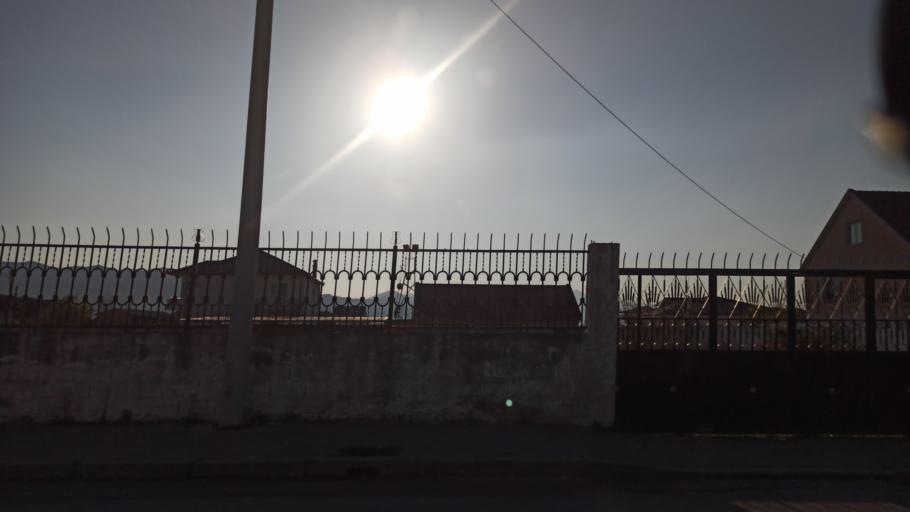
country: AL
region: Shkoder
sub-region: Rrethi i Shkodres
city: Shkoder
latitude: 42.0867
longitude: 19.5085
